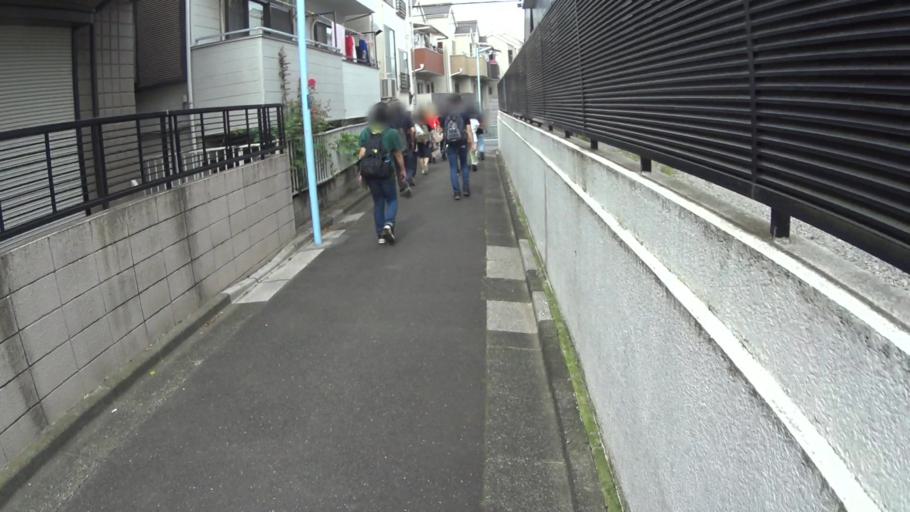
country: JP
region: Tokyo
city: Musashino
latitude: 35.7141
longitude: 139.6094
